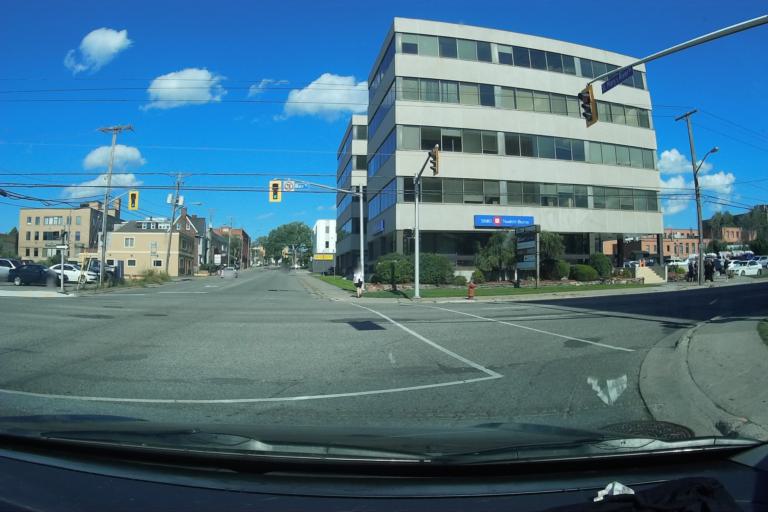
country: CA
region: Ontario
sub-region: Algoma
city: Sault Ste. Marie
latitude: 46.5112
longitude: -84.3354
